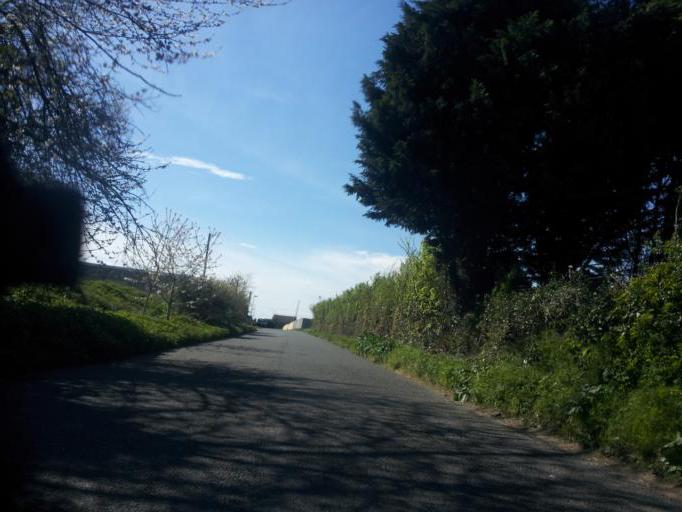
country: GB
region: England
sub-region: Kent
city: Rainham
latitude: 51.3681
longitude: 0.6296
